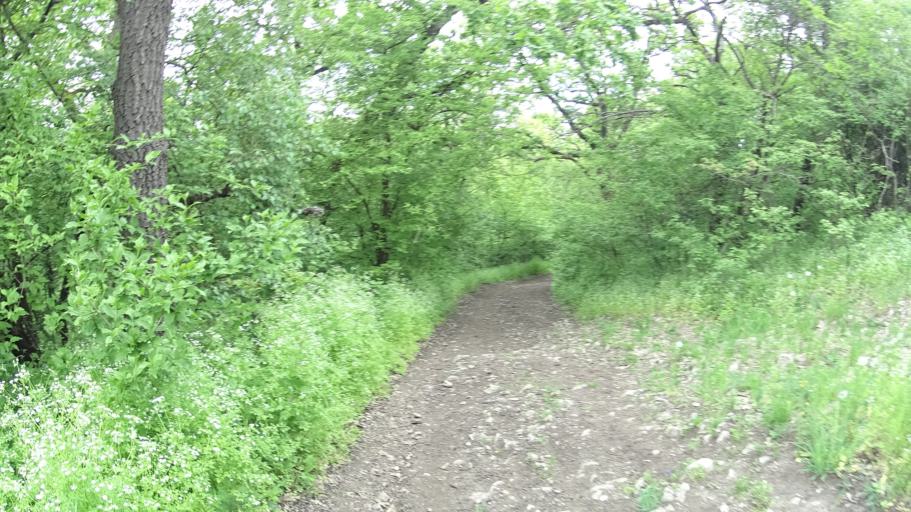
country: HU
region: Pest
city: Acsa
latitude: 47.8220
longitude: 19.3056
